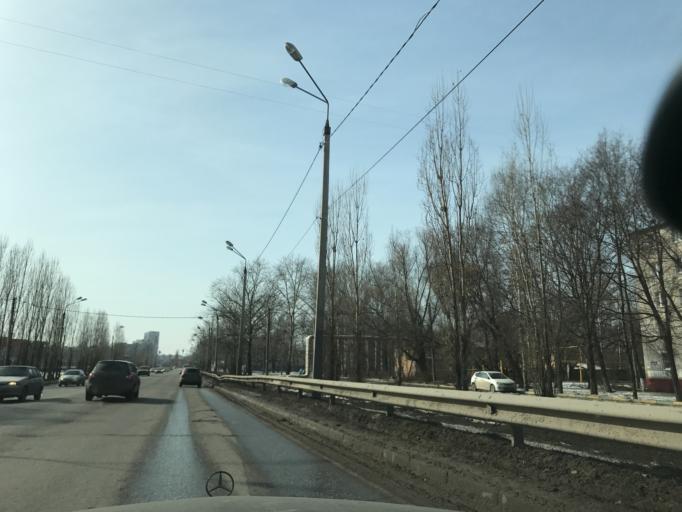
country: RU
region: Nizjnij Novgorod
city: Gorbatovka
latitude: 56.2651
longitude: 43.8722
